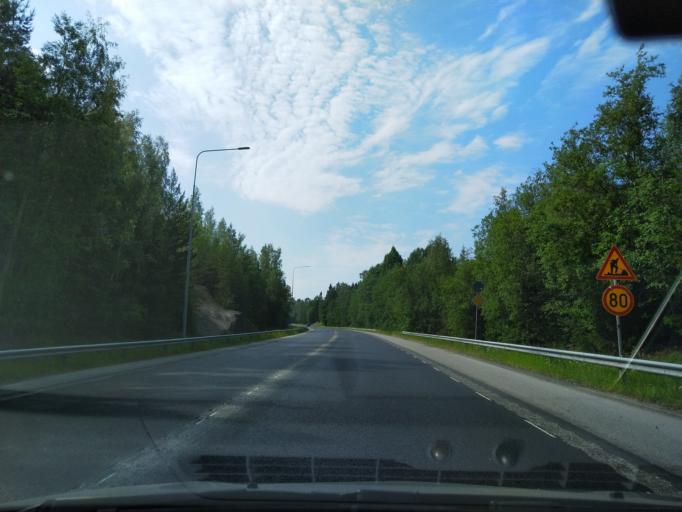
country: FI
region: Uusimaa
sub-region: Helsinki
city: Vihti
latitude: 60.3756
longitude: 24.3168
